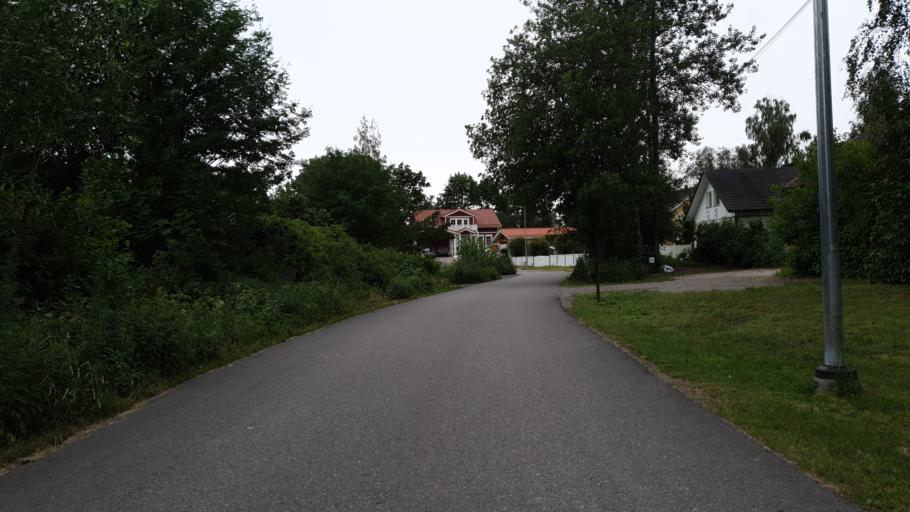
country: FI
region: Uusimaa
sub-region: Helsinki
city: Helsinki
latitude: 60.2778
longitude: 24.9165
